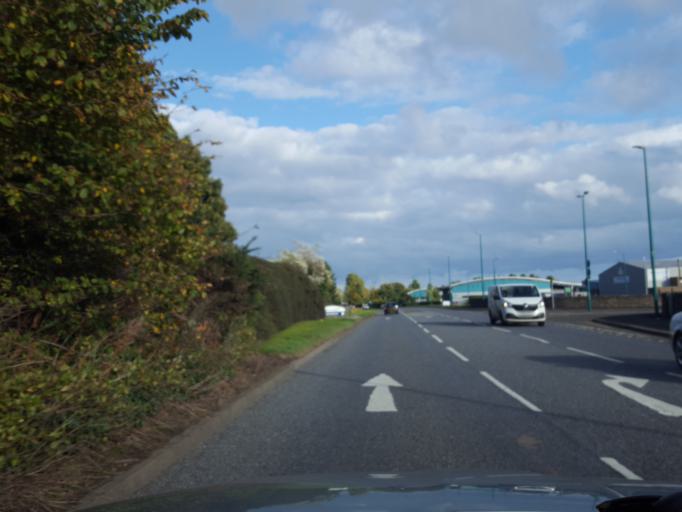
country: GB
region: Scotland
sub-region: Dundee City
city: Dundee
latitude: 56.4544
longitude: -3.0154
